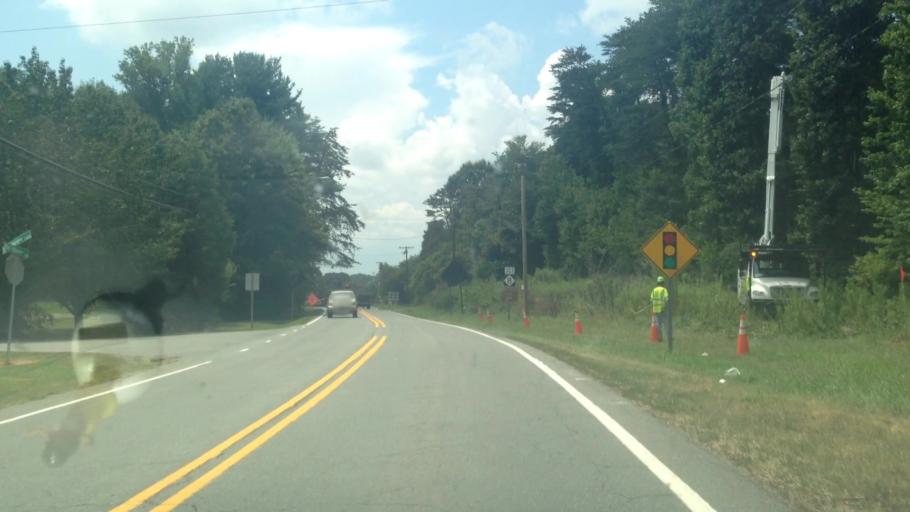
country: US
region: North Carolina
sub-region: Forsyth County
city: Rural Hall
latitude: 36.1946
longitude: -80.2519
